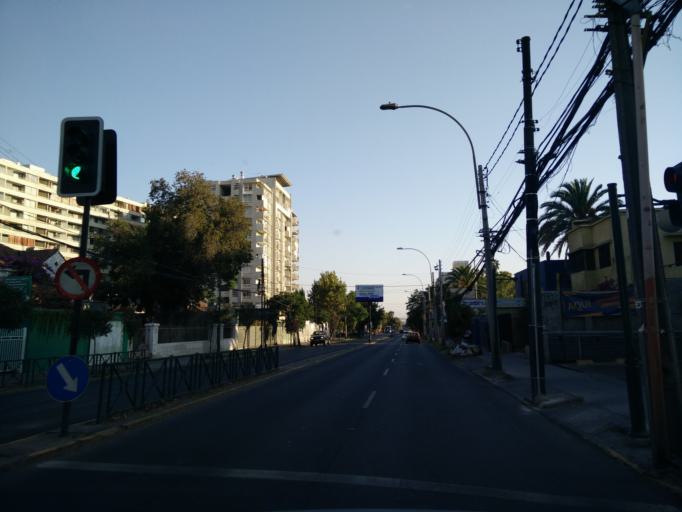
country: CL
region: Santiago Metropolitan
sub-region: Provincia de Santiago
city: Villa Presidente Frei, Nunoa, Santiago, Chile
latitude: -33.4557
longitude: -70.6052
